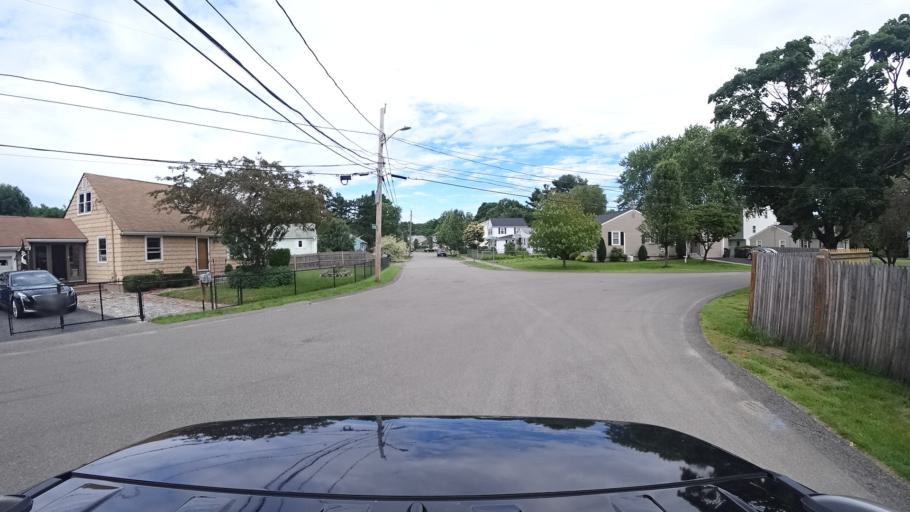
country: US
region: Massachusetts
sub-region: Norfolk County
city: Dedham
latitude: 42.2277
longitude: -71.1404
